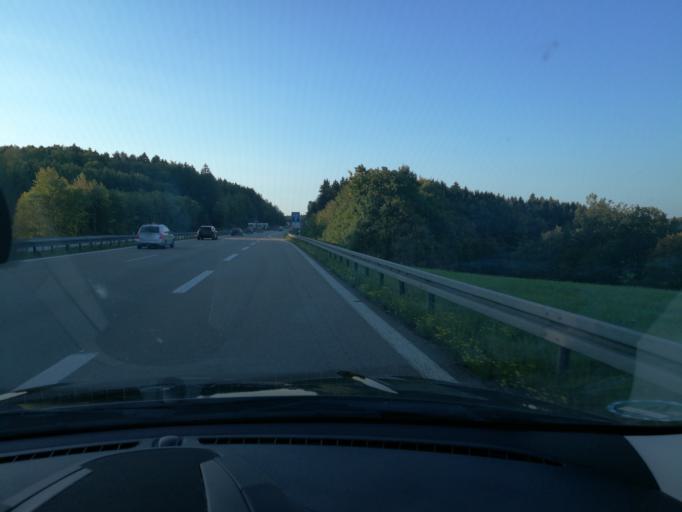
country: DE
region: Bavaria
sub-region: Upper Palatinate
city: Velburg
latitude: 49.2562
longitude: 11.6099
